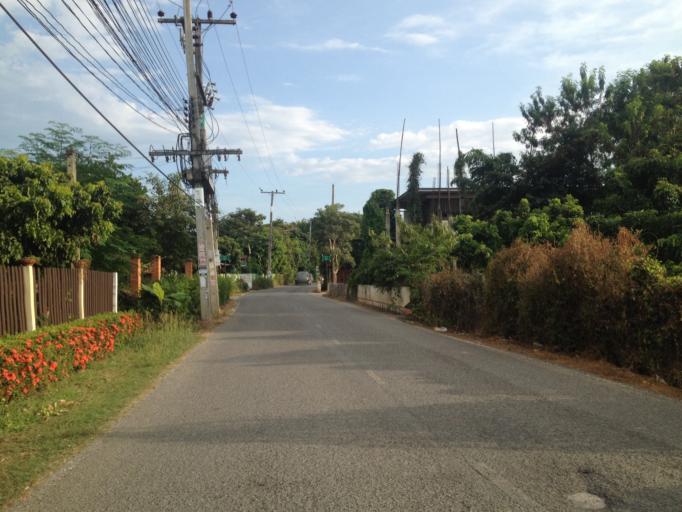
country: TH
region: Chiang Mai
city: Saraphi
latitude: 18.6938
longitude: 98.9876
